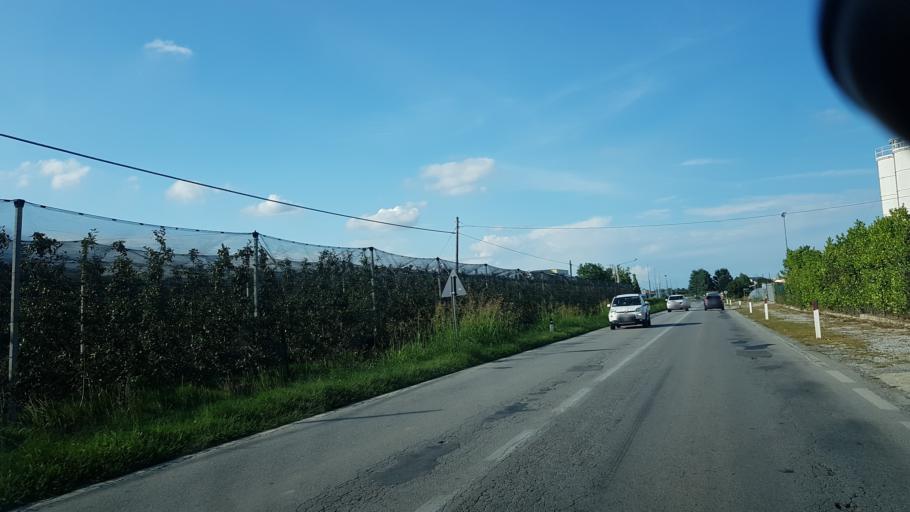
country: IT
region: Piedmont
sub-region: Provincia di Cuneo
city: Costiglione Saluzzo
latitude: 44.5459
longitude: 7.4901
